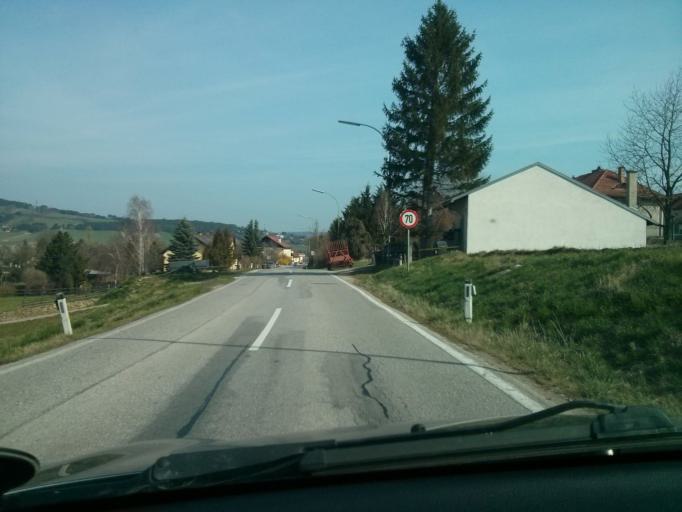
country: AT
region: Lower Austria
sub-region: Politischer Bezirk Baden
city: Berndorf
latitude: 47.9255
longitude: 16.0949
